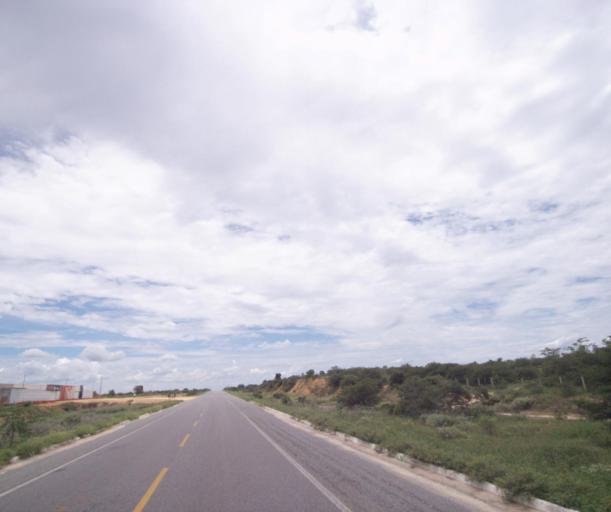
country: BR
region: Bahia
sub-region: Carinhanha
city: Carinhanha
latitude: -14.2973
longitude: -43.7855
